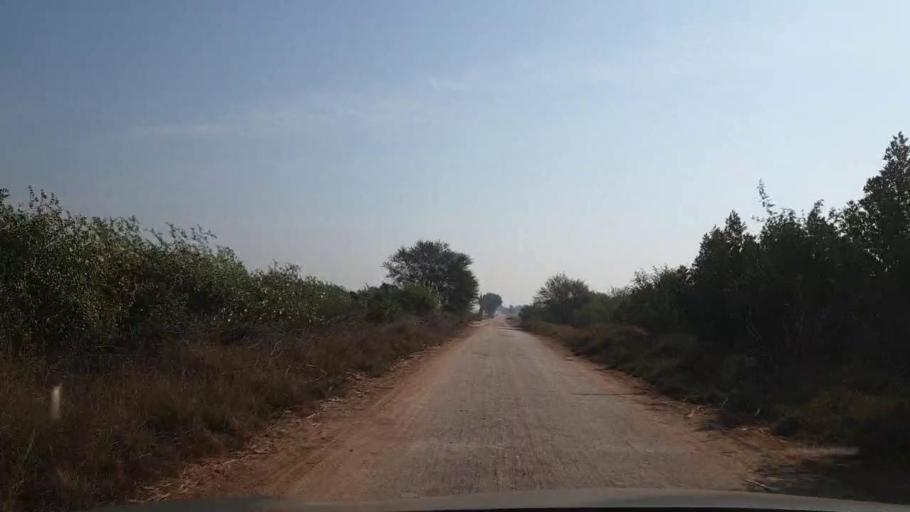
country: PK
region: Sindh
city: Tando Allahyar
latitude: 25.5935
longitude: 68.7308
